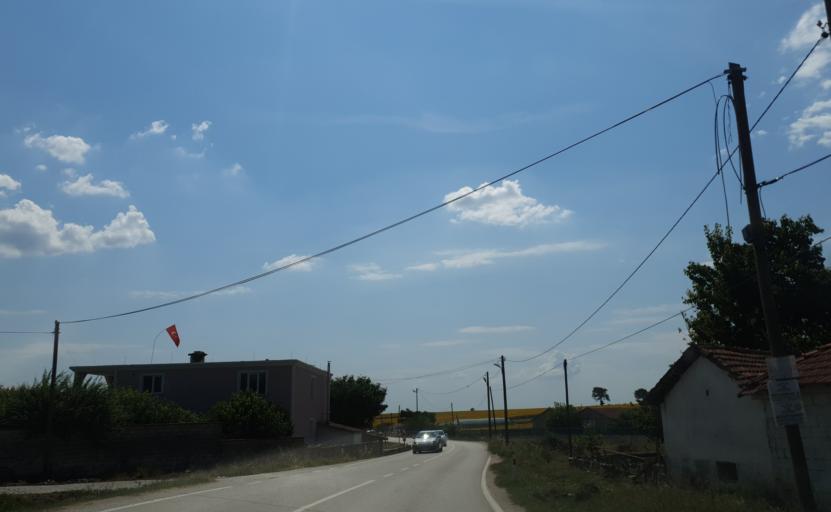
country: TR
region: Tekirdag
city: Beyazkoy
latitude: 41.4553
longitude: 27.6432
